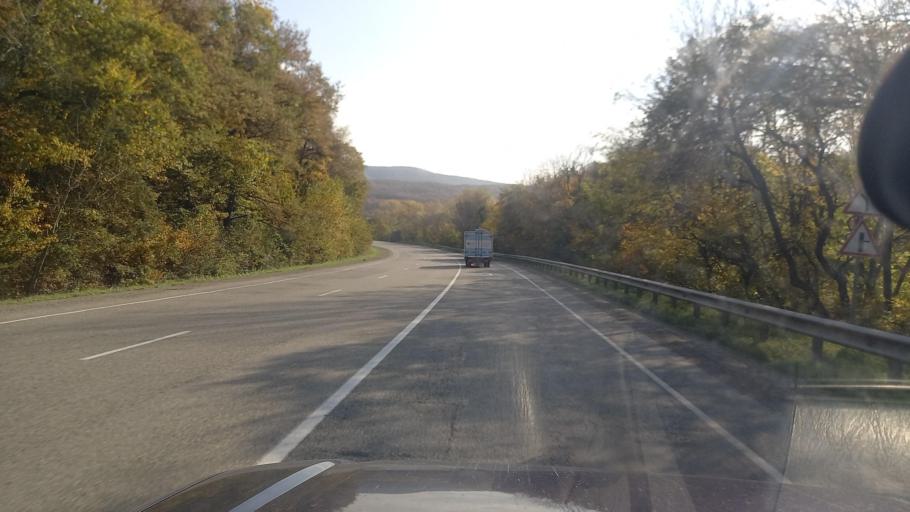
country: RU
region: Krasnodarskiy
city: Verkhnebakanskiy
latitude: 44.8415
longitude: 37.7048
